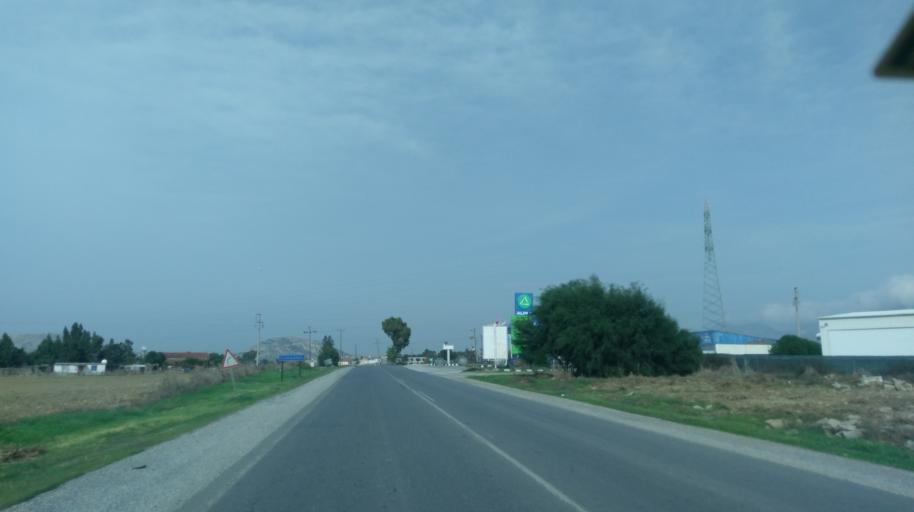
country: CY
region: Lefkosia
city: Mammari
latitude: 35.2245
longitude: 33.1743
